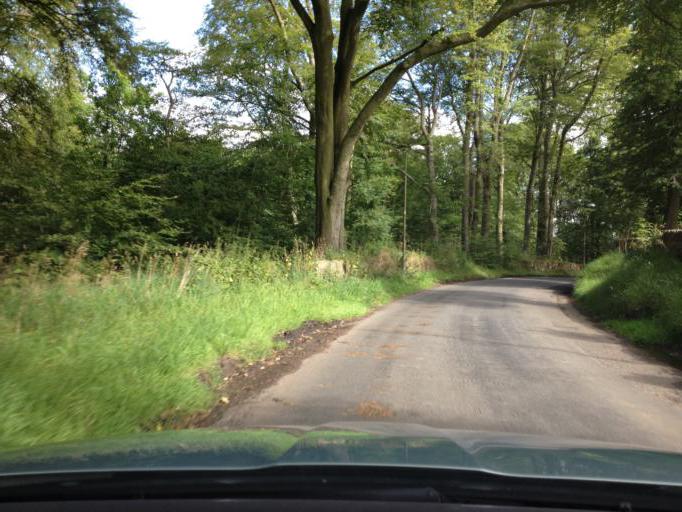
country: GB
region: Scotland
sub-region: West Lothian
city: Armadale
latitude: 55.9216
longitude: -3.6992
